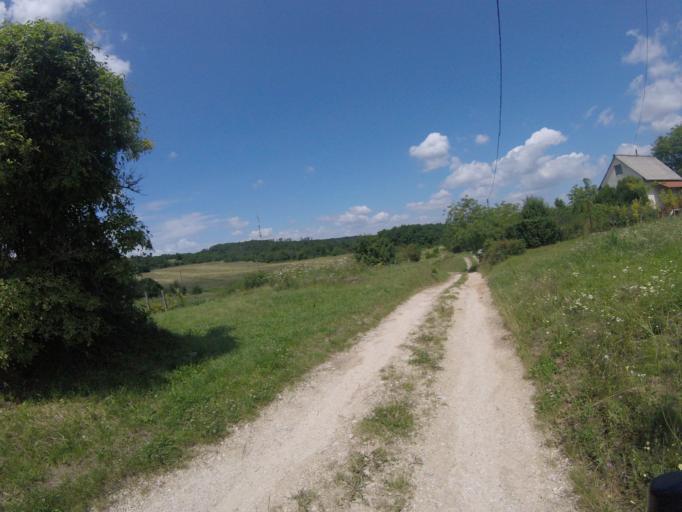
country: HU
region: Zala
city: Nagykanizsa
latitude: 46.5547
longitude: 17.0341
